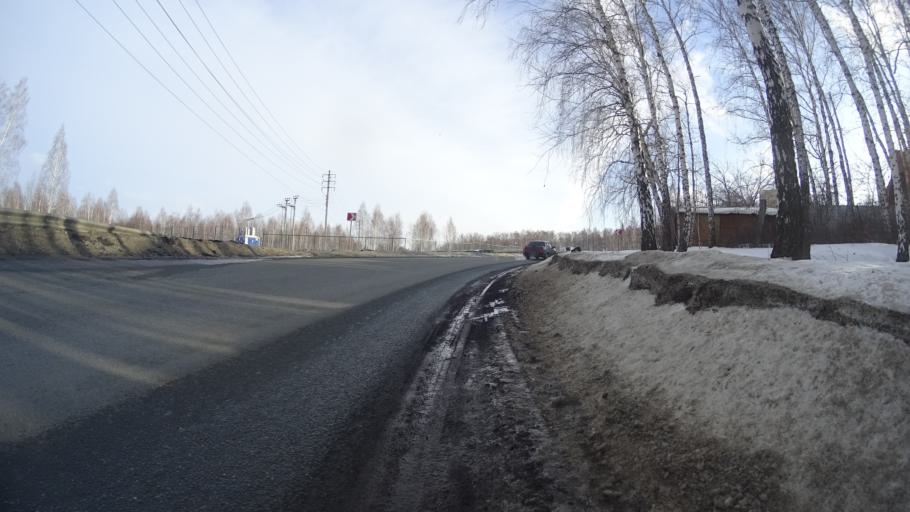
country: RU
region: Chelyabinsk
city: Sargazy
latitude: 55.1285
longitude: 61.2886
